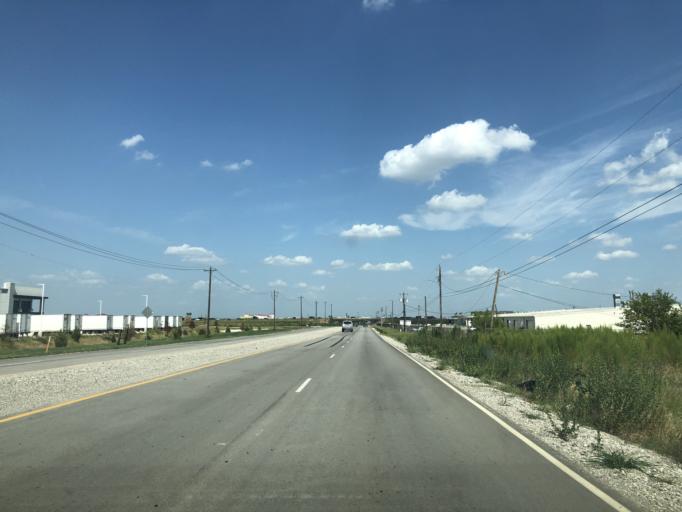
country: US
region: Texas
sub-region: Tarrant County
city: Haslet
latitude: 32.9333
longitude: -97.3215
